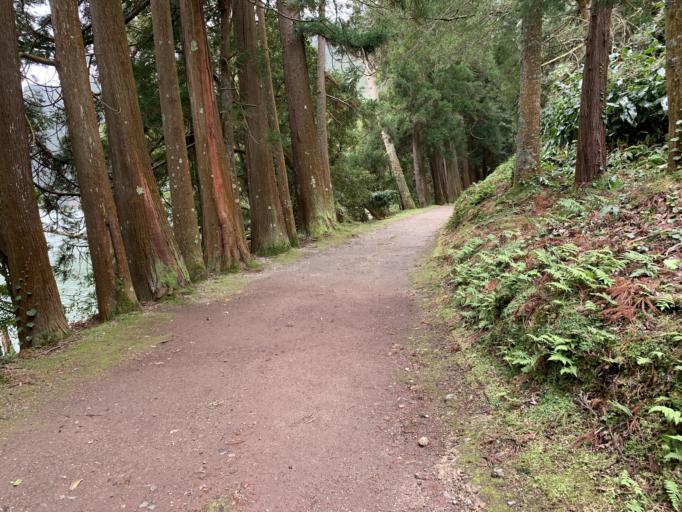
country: PT
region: Azores
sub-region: Povoacao
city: Furnas
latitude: 37.7640
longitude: -25.3339
